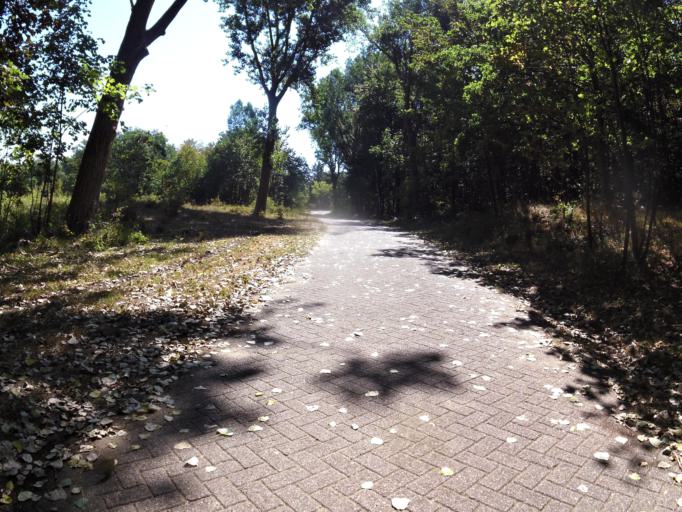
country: NL
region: North Holland
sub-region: Gemeente Beverwijk
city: Beverwijk
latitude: 52.5140
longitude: 4.6153
